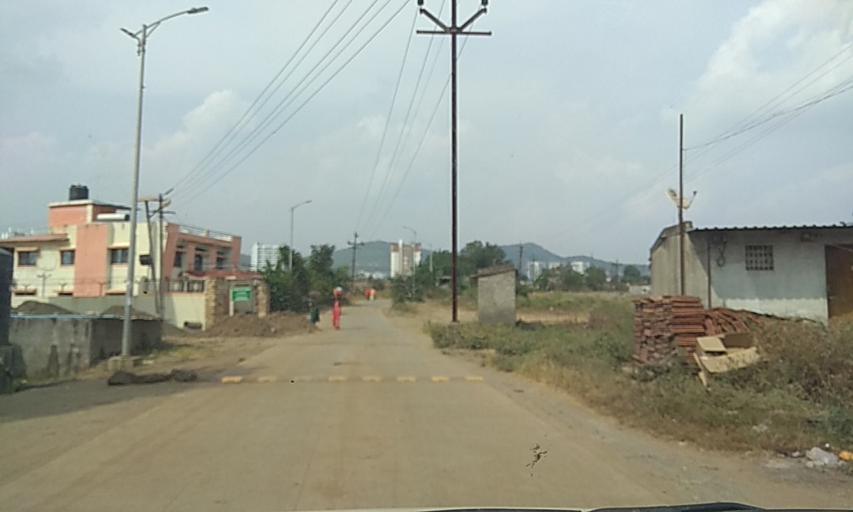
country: IN
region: Maharashtra
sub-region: Pune Division
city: Pimpri
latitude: 18.5831
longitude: 73.7062
